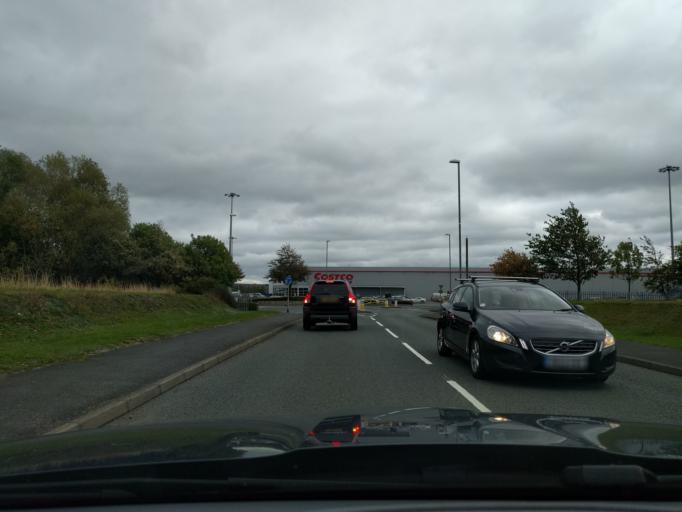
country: GB
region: England
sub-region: Newcastle upon Tyne
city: Benwell
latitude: 54.9613
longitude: -1.6618
